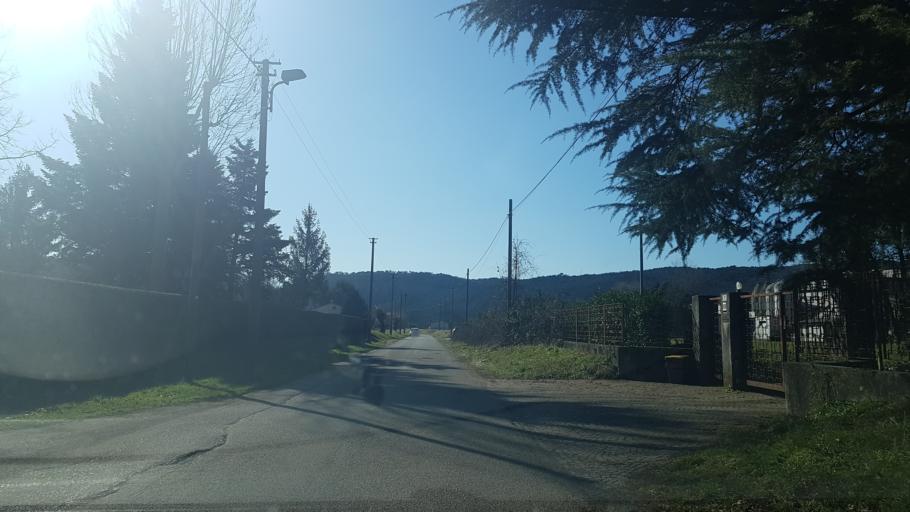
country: IT
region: Friuli Venezia Giulia
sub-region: Provincia di Gorizia
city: Savogna d'Isonzo
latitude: 45.8980
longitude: 13.5842
